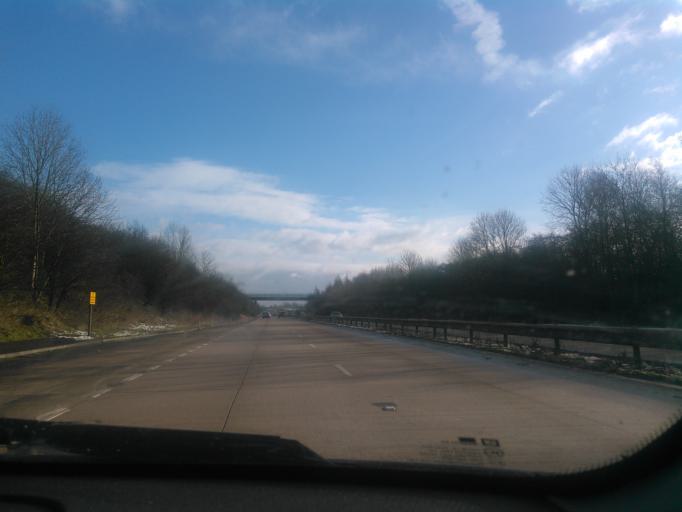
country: GB
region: England
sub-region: Staffordshire
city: Cheadle
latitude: 52.9402
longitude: -1.9938
